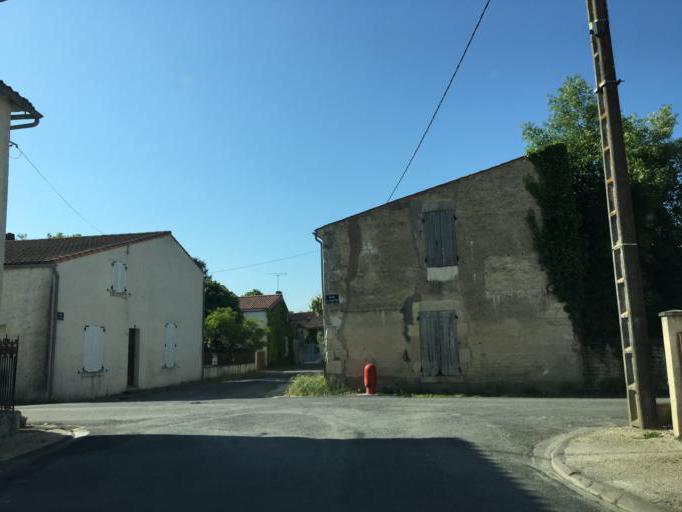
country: FR
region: Poitou-Charentes
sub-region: Departement des Deux-Sevres
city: Beauvoir-sur-Niort
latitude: 46.0952
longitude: -0.5066
